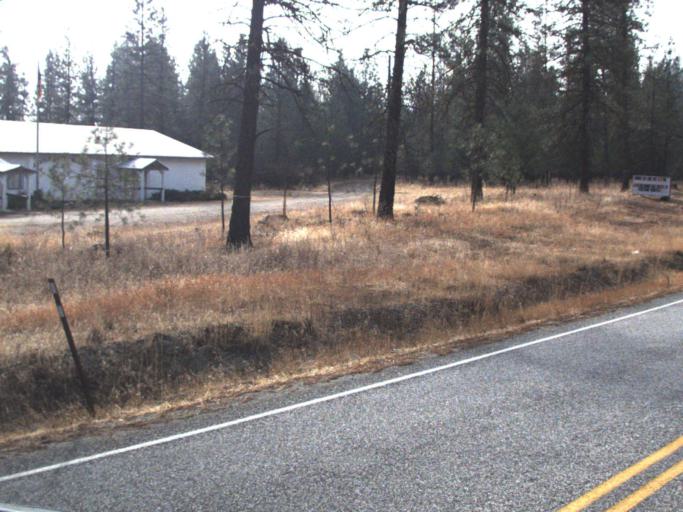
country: US
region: Washington
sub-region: Stevens County
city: Kettle Falls
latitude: 48.7731
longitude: -118.1430
